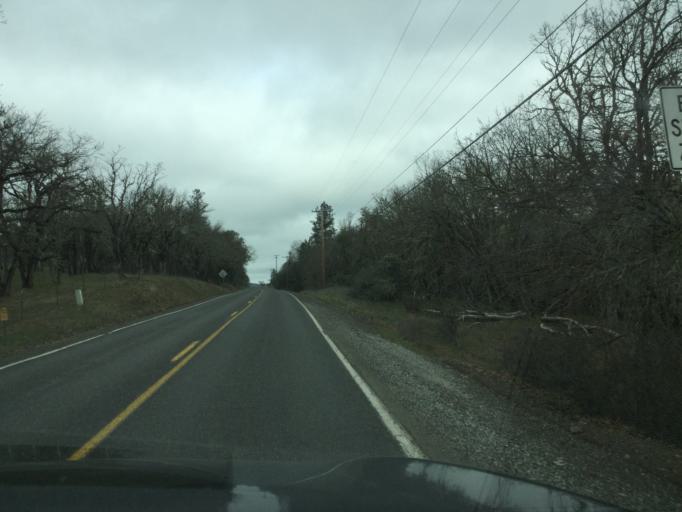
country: US
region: Oregon
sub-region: Jackson County
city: Central Point
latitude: 42.3896
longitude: -122.9866
